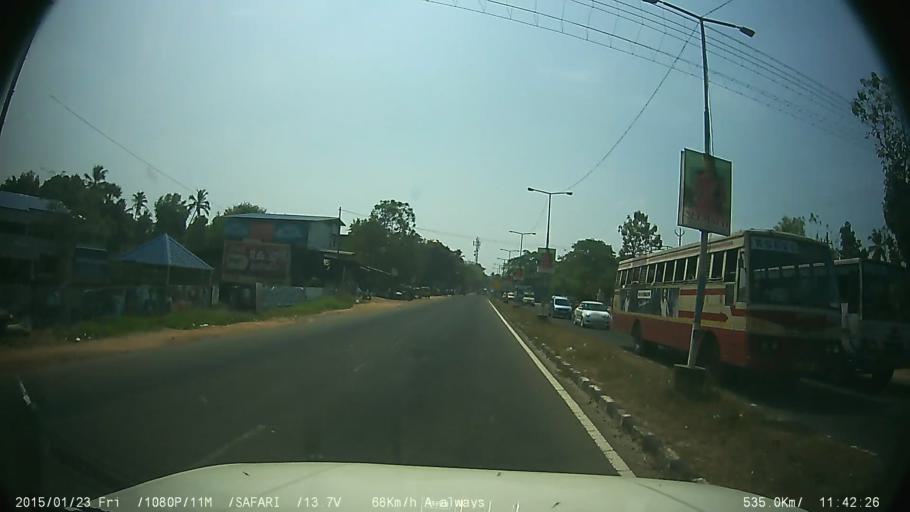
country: IN
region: Kerala
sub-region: Alappuzha
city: Kutiatodu
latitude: 9.7715
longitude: 76.3182
